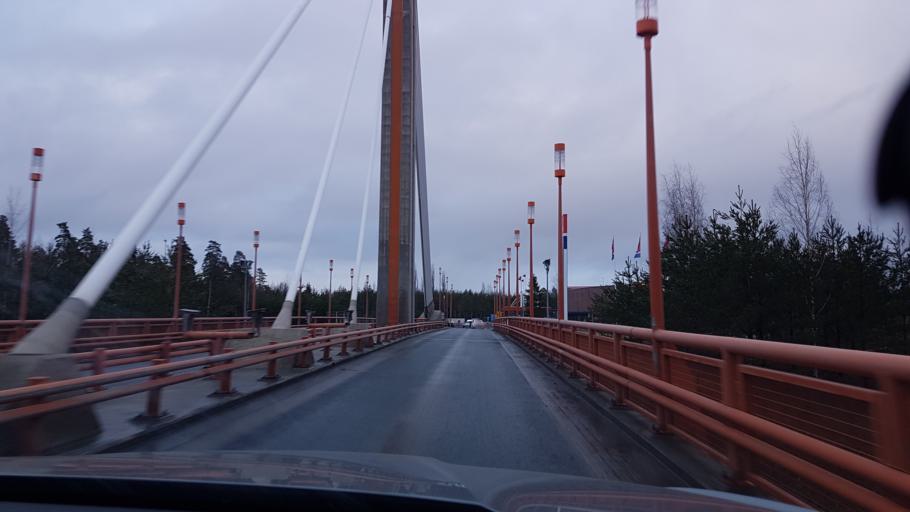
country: FI
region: Pirkanmaa
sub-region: Etelae-Pirkanmaa
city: Viiala
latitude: 61.2548
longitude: 23.8360
